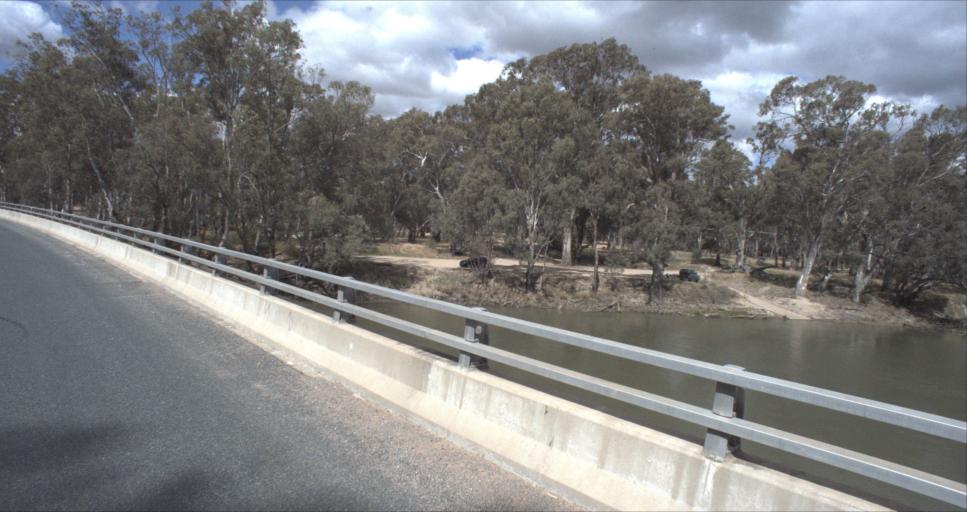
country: AU
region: New South Wales
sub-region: Leeton
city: Leeton
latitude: -34.6390
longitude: 146.3736
